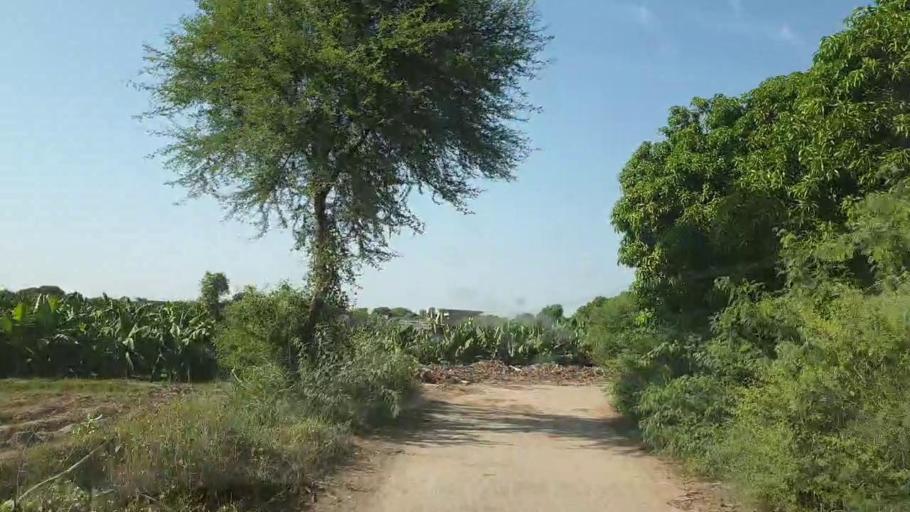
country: PK
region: Sindh
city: Tando Jam
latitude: 25.3477
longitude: 68.5816
